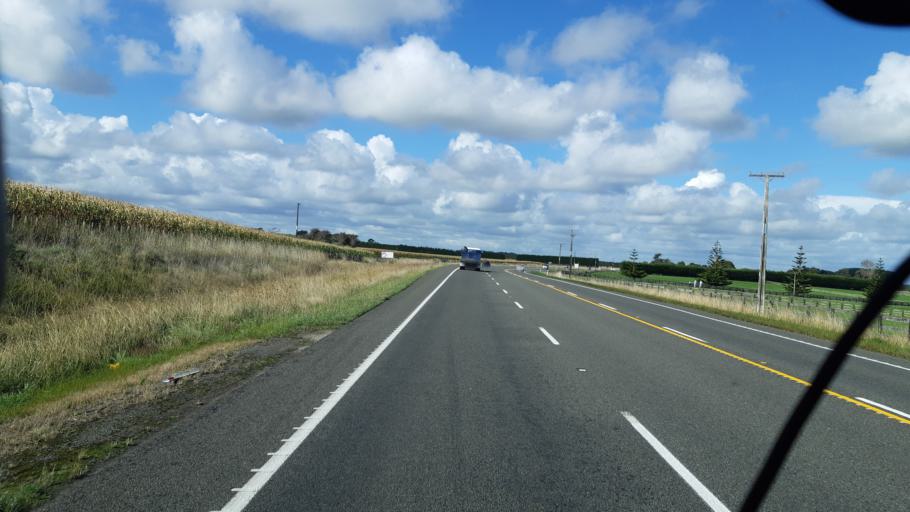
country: NZ
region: Manawatu-Wanganui
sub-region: Wanganui District
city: Wanganui
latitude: -39.9817
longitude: 175.1479
